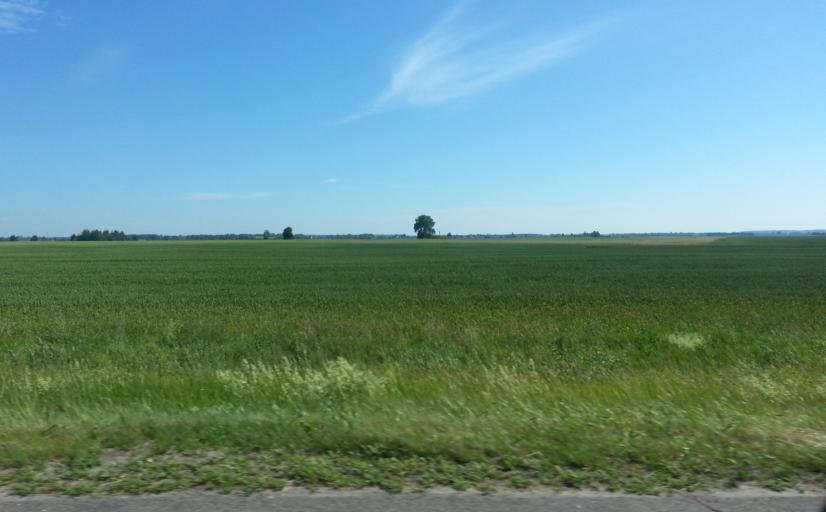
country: LT
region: Vilnius County
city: Ukmerge
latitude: 55.3716
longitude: 24.7249
